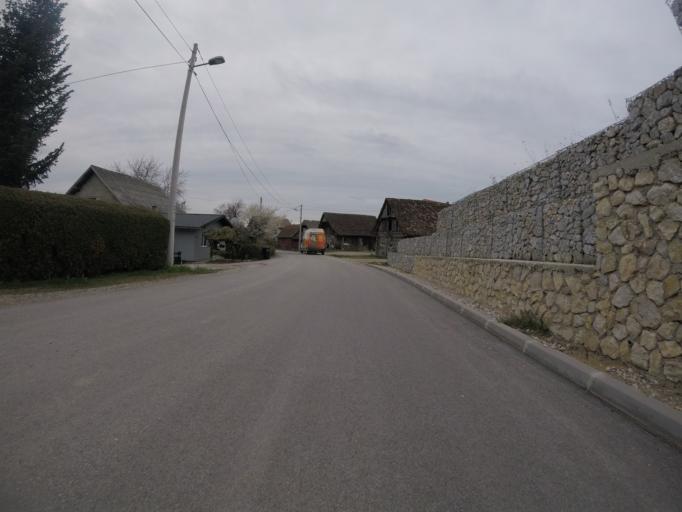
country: HR
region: Grad Zagreb
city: Strmec
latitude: 45.6271
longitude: 15.9347
